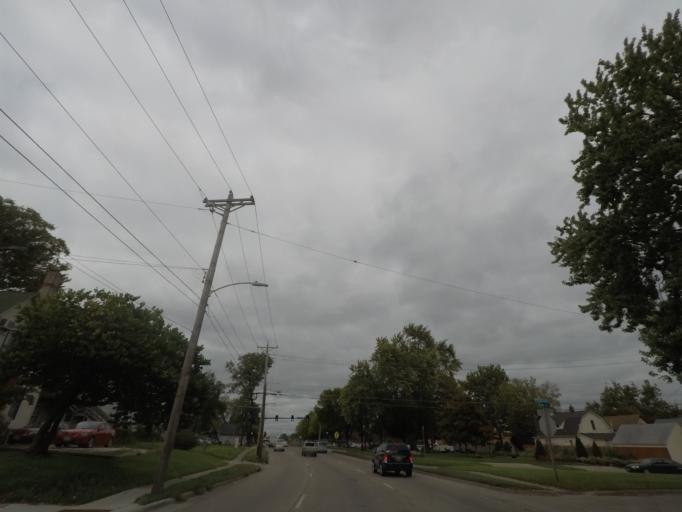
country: US
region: Iowa
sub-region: Polk County
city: Des Moines
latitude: 41.5911
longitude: -93.5943
